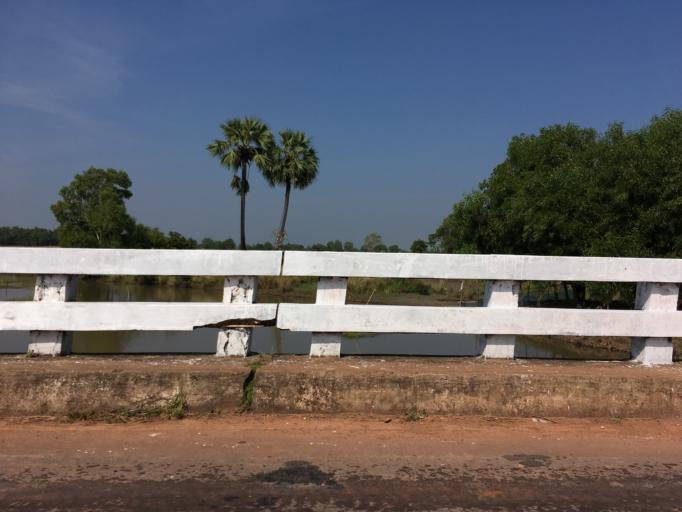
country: MM
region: Mon
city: Martaban
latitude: 16.6615
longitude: 97.7437
